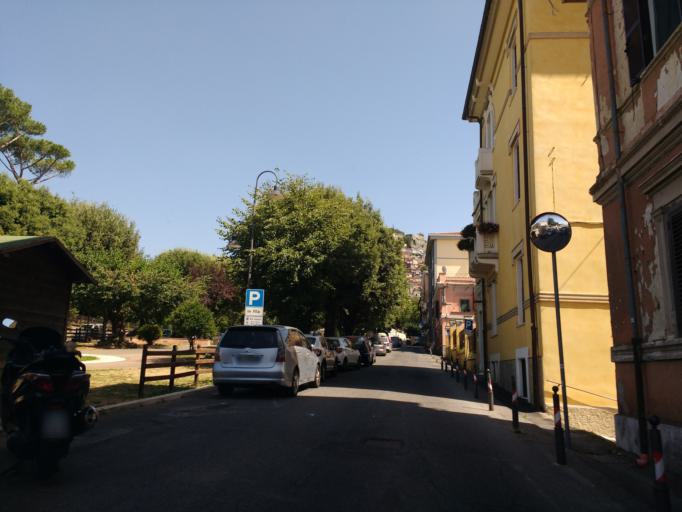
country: IT
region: Latium
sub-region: Citta metropolitana di Roma Capitale
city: Rocca di Papa
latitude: 41.7629
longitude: 12.7049
